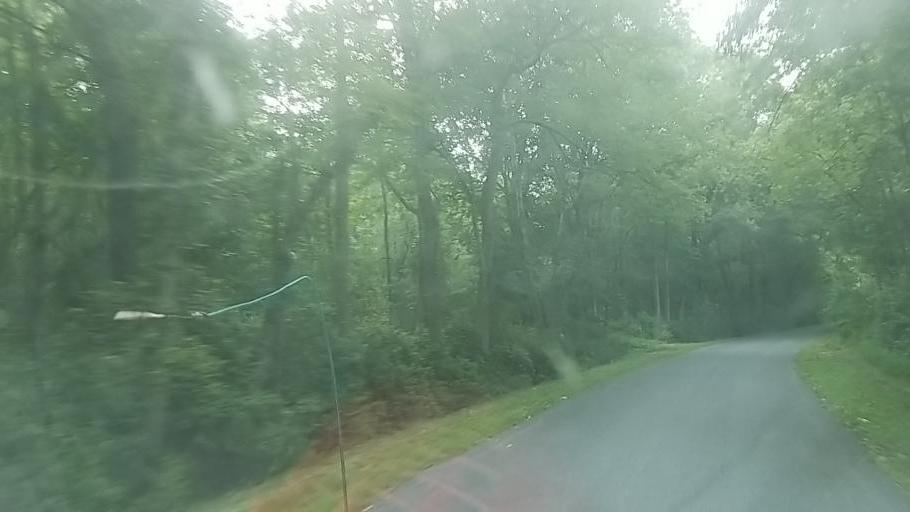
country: US
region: Maryland
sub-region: Wicomico County
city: Pittsville
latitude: 38.4424
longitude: -75.3407
